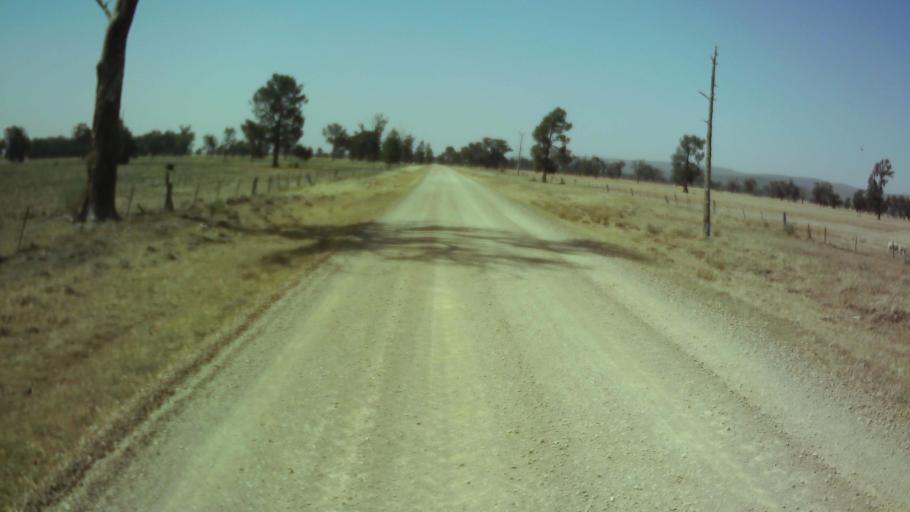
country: AU
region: New South Wales
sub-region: Weddin
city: Grenfell
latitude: -34.0263
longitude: 147.9135
